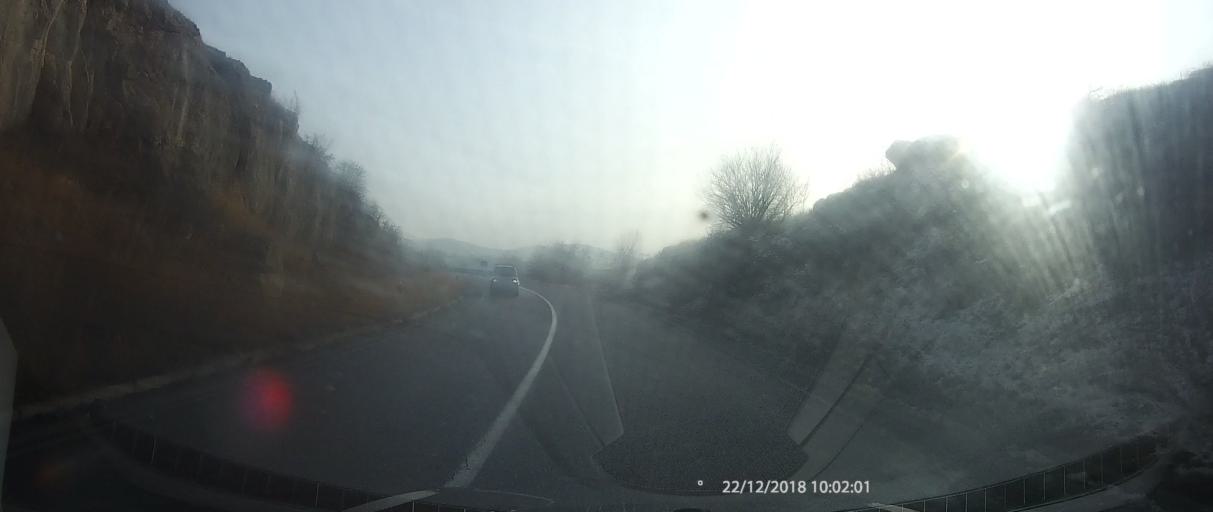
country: MK
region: Opstina Rankovce
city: Rankovce
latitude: 42.1463
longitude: 22.0032
